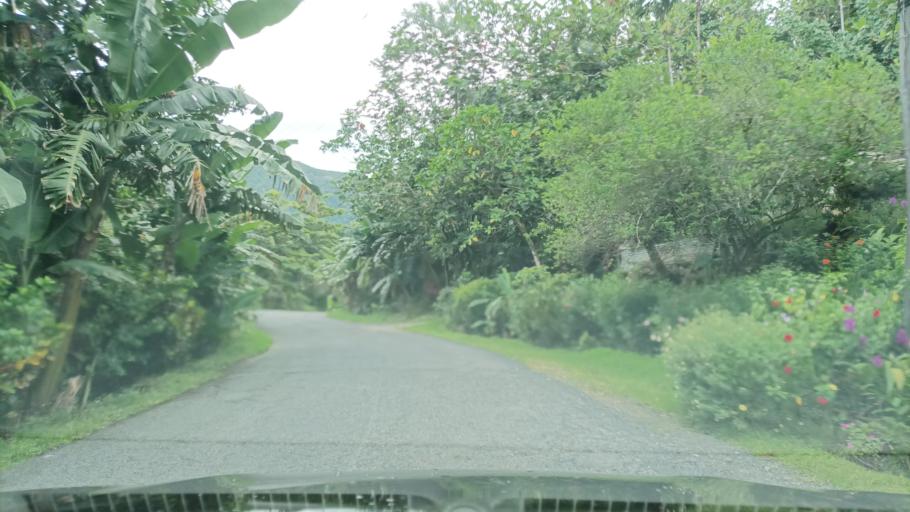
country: FM
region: Pohnpei
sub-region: Kolonia Municipality
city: Kolonia
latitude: 6.9489
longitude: 158.2751
